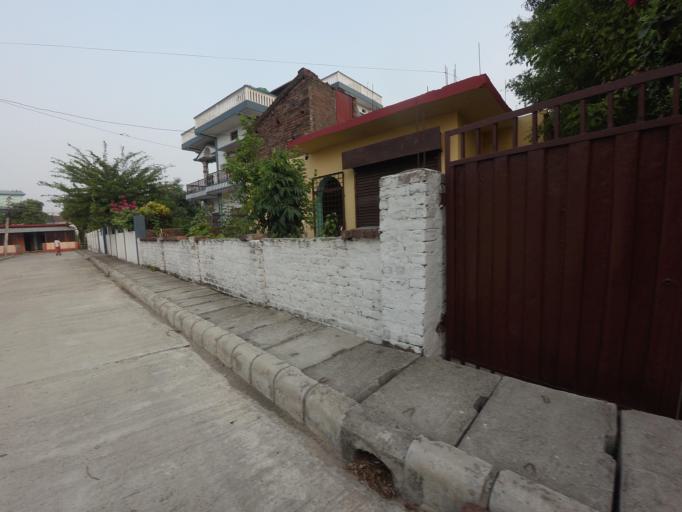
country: NP
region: Western Region
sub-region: Lumbini Zone
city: Bhairahawa
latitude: 27.5128
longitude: 83.4617
